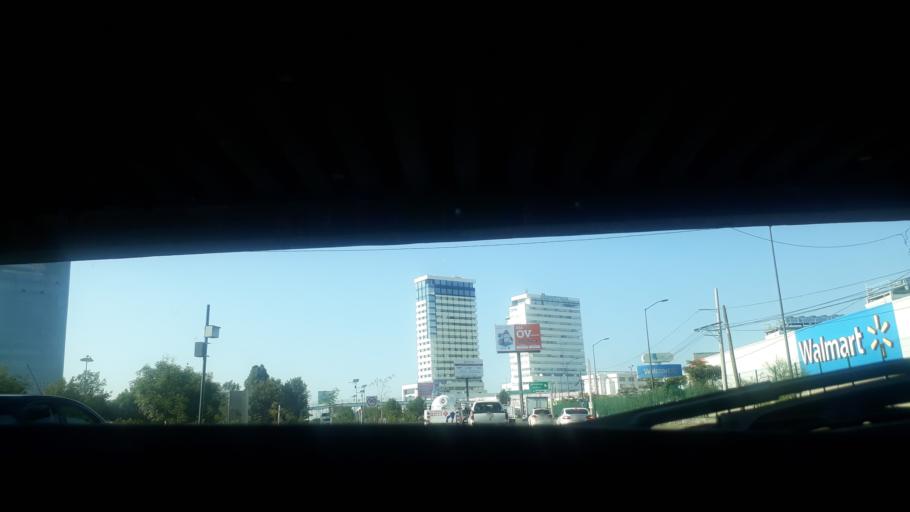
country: MX
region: Puebla
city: Tlazcalancingo
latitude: 19.0164
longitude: -98.2643
